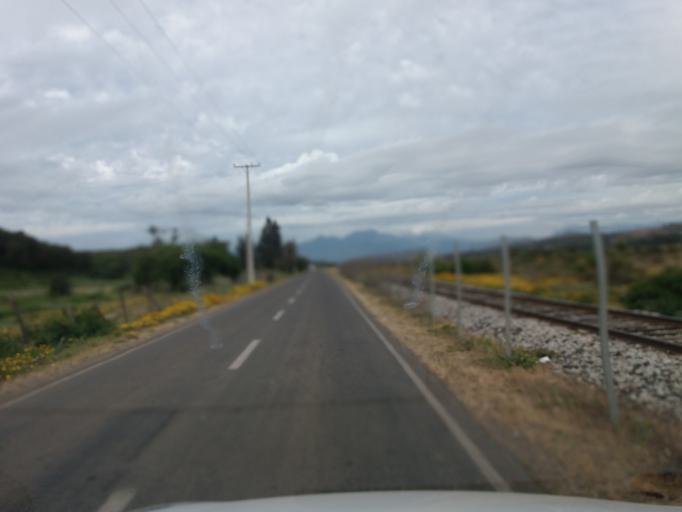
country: CL
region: Valparaiso
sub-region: Provincia de Marga Marga
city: Quilpue
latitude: -32.9161
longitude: -71.4214
